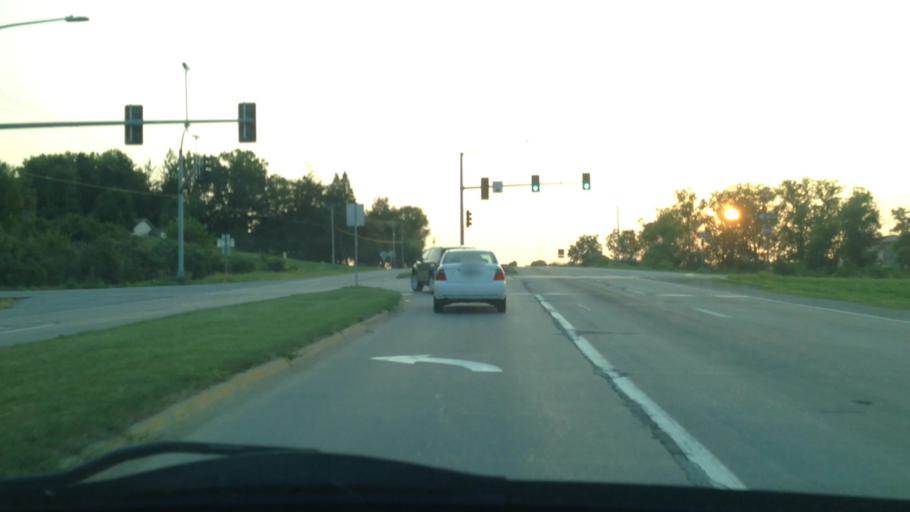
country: US
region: Iowa
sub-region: Johnson County
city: Coralville
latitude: 41.6571
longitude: -91.5993
